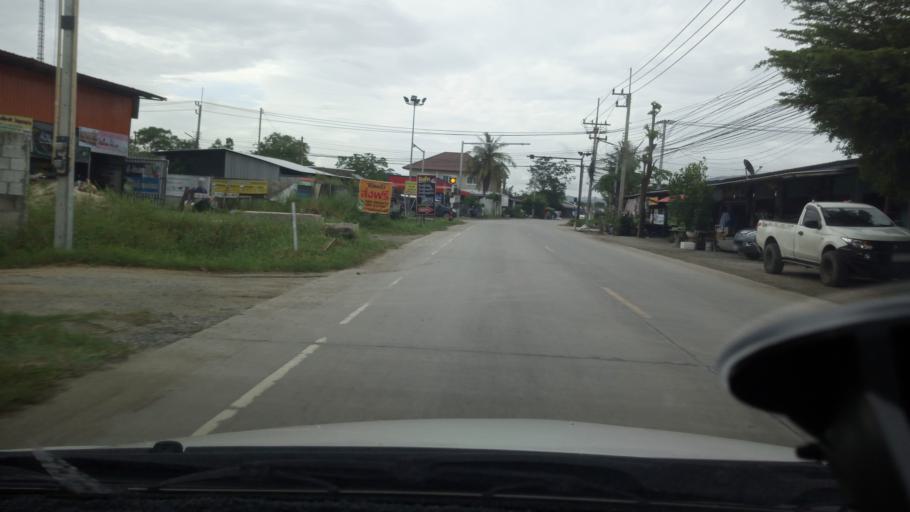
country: TH
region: Chon Buri
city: Ban Bueng
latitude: 13.3635
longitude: 101.0598
